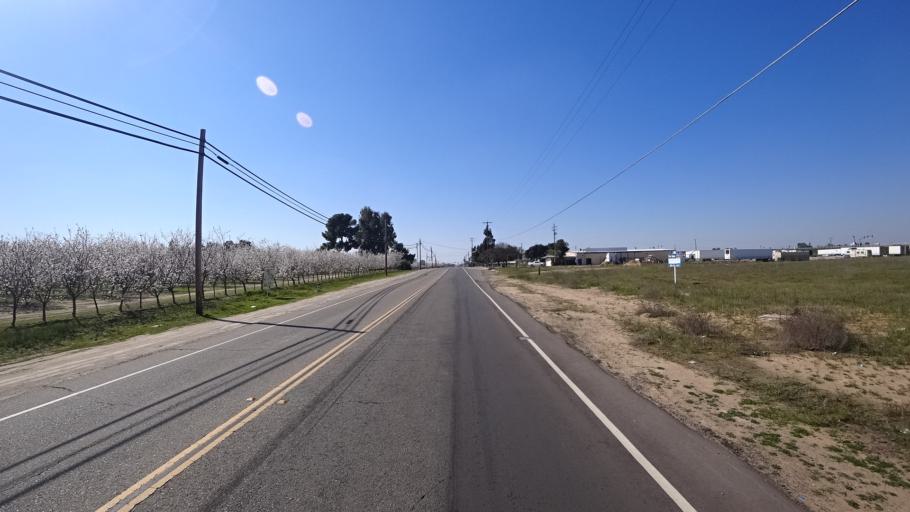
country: US
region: California
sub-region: Fresno County
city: West Park
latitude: 36.7357
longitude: -119.8379
